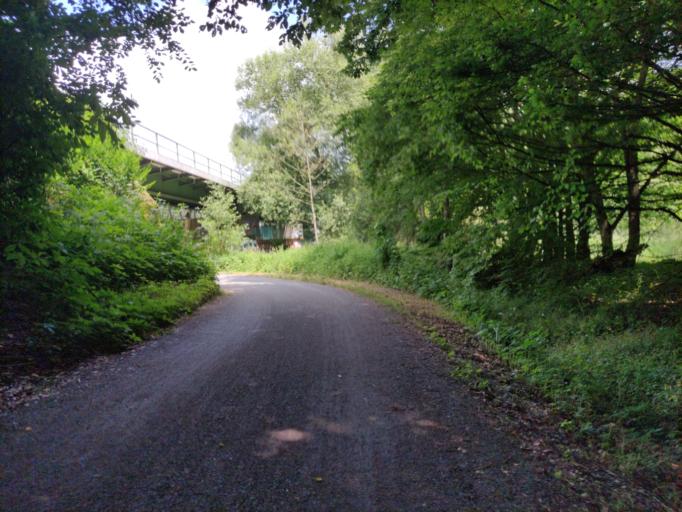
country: DE
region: Lower Saxony
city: Hildesheim
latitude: 52.1268
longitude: 9.9655
